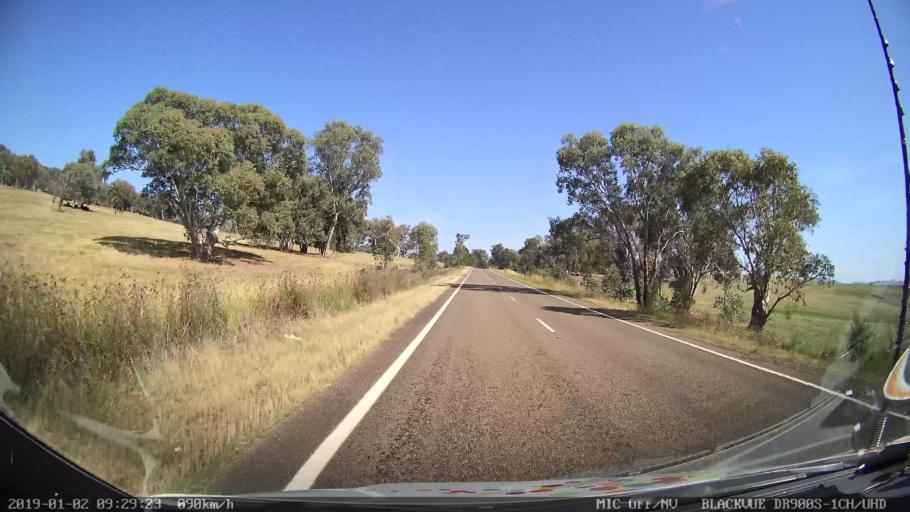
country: AU
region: New South Wales
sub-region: Tumut Shire
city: Tumut
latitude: -35.3392
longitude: 148.2430
